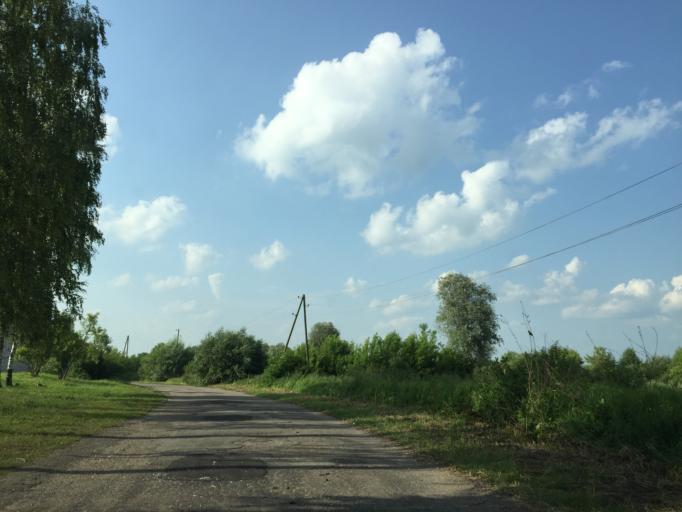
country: LV
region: Jelgava
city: Jelgava
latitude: 56.6641
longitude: 23.7163
